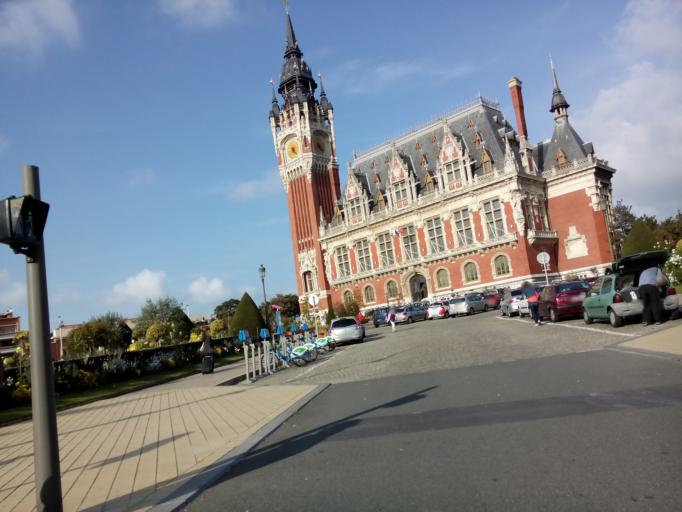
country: FR
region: Nord-Pas-de-Calais
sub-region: Departement du Pas-de-Calais
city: Calais
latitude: 50.9519
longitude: 1.8536
